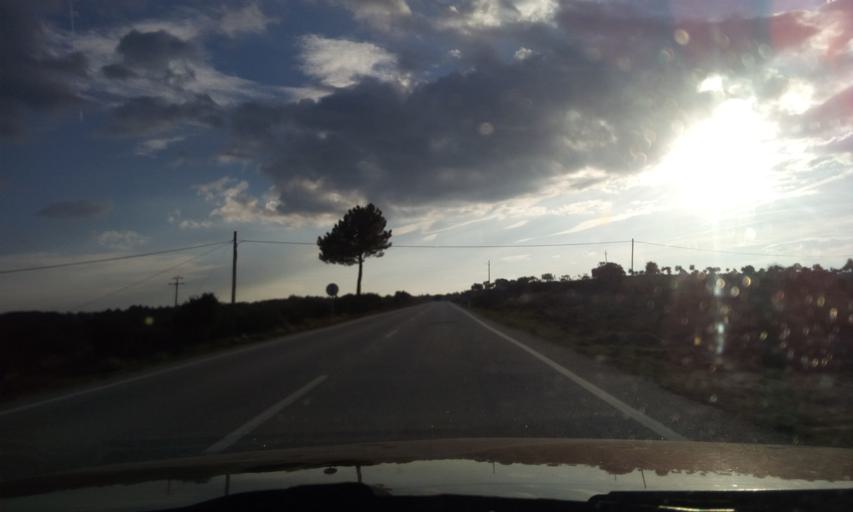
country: PT
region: Guarda
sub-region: Pinhel
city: Pinhel
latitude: 40.6666
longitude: -6.9589
